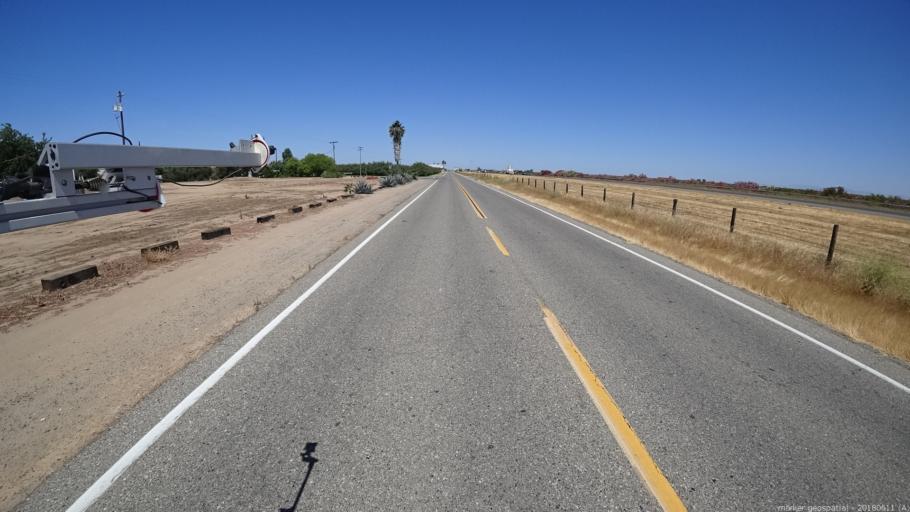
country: US
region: California
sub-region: Madera County
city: Madera Acres
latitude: 37.0250
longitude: -120.1367
